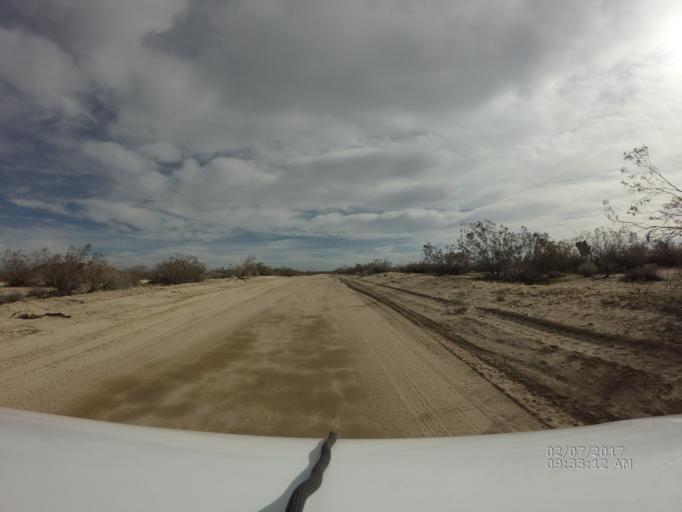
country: US
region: California
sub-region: San Bernardino County
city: Pinon Hills
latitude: 34.5189
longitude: -117.7394
